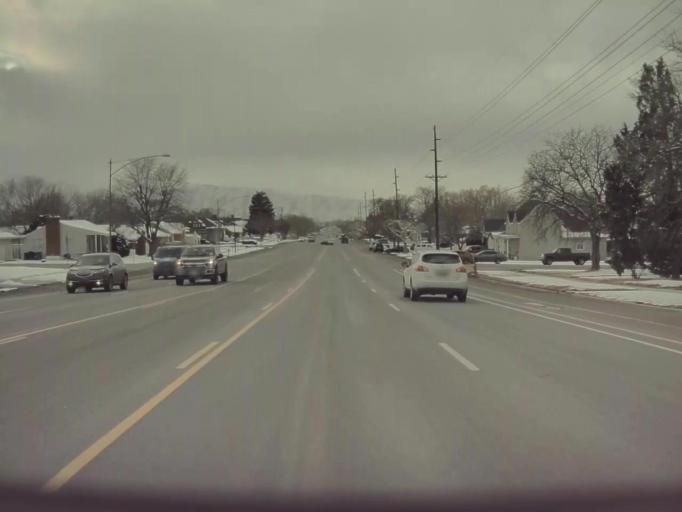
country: US
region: Utah
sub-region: Utah County
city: Spanish Fork
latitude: 40.1099
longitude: -111.6451
